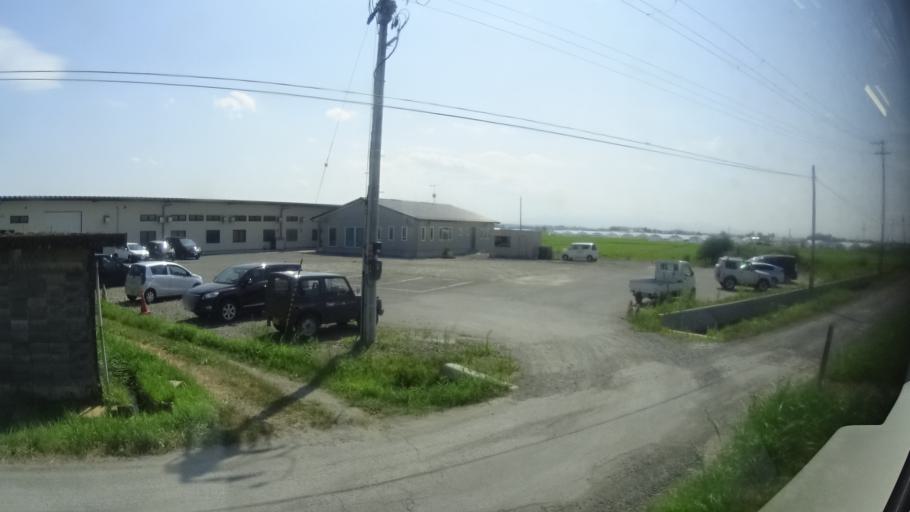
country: JP
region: Miyagi
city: Wakuya
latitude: 38.5498
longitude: 141.0976
